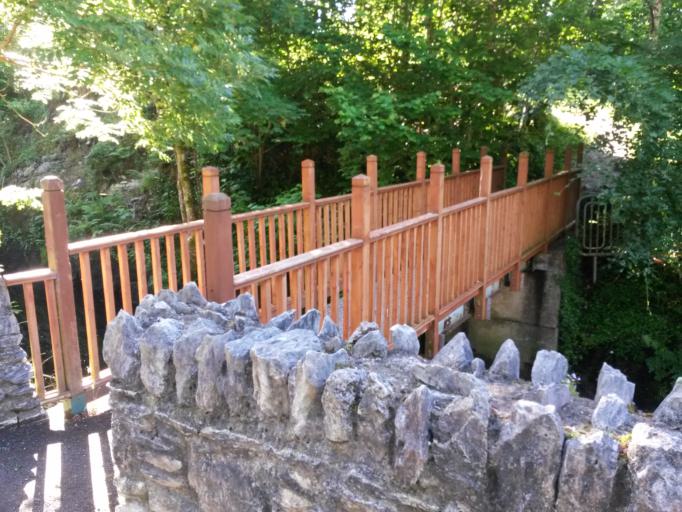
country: IE
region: Munster
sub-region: Ciarrai
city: Kenmare
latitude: 51.8804
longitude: -9.5869
